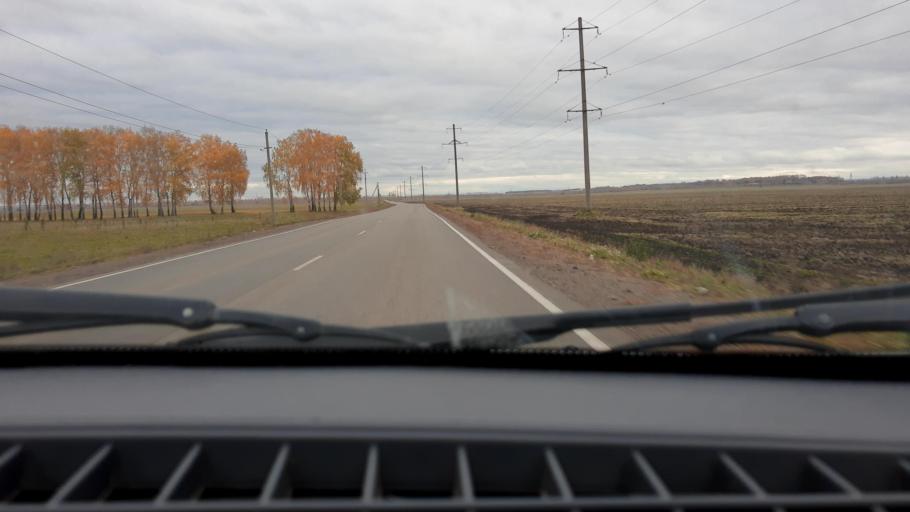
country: RU
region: Bashkortostan
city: Kabakovo
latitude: 54.5451
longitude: 56.0443
